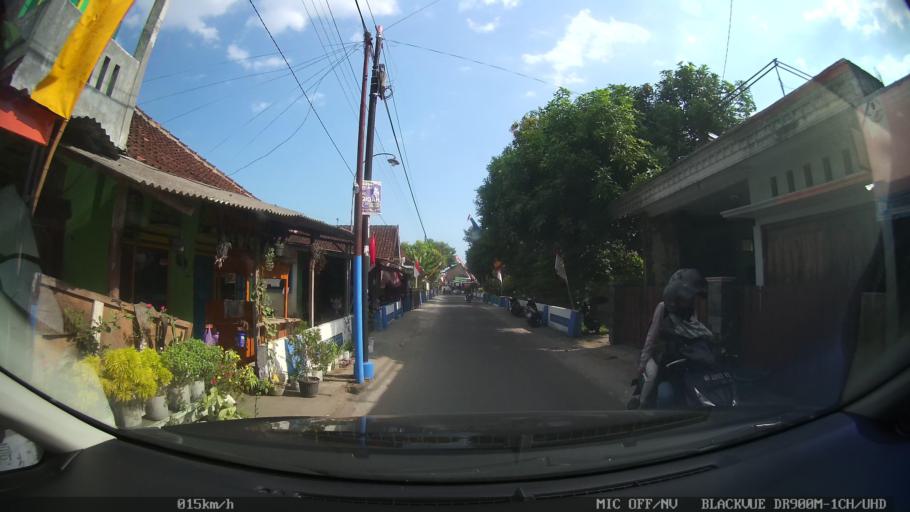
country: ID
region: Daerah Istimewa Yogyakarta
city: Gamping Lor
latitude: -7.7941
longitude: 110.3439
